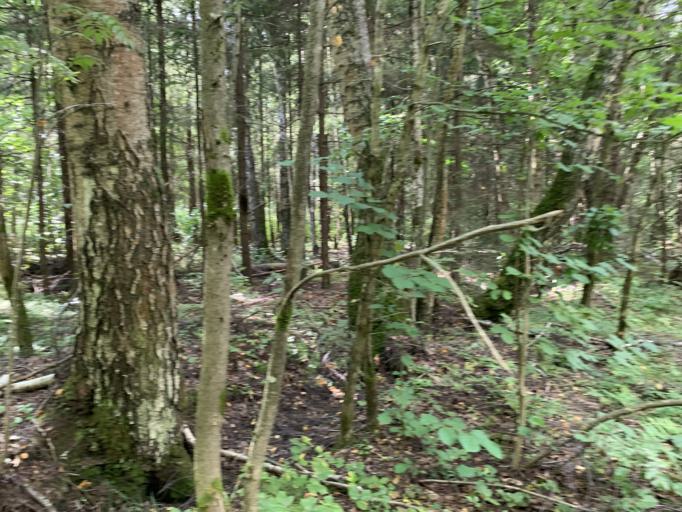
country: RU
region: Moskovskaya
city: Podosinki
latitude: 56.1779
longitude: 37.5691
